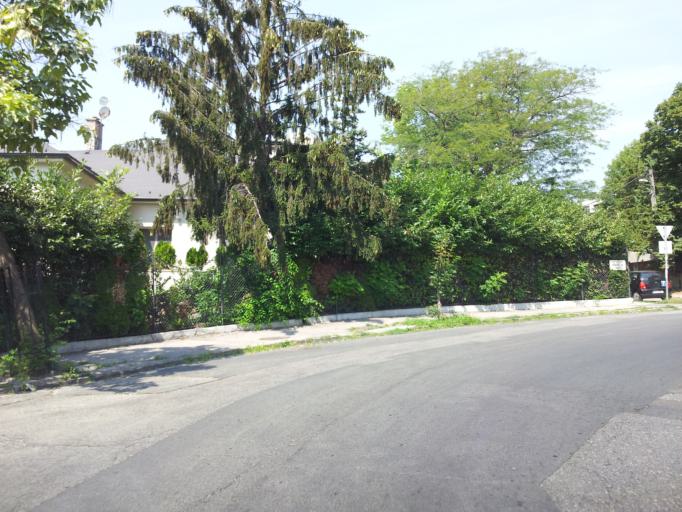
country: HU
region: Budapest
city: Budapest XI. keruelet
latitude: 47.4838
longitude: 19.0389
